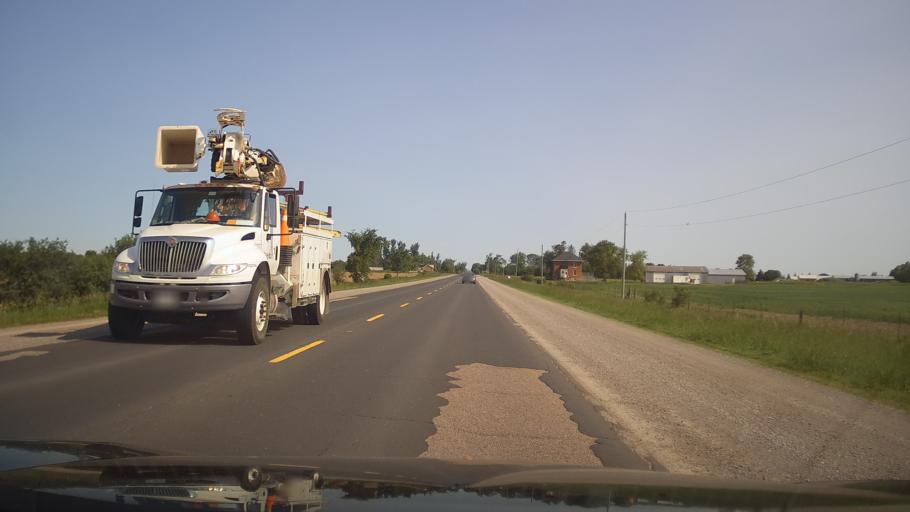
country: CA
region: Ontario
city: Omemee
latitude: 44.3266
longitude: -78.6856
